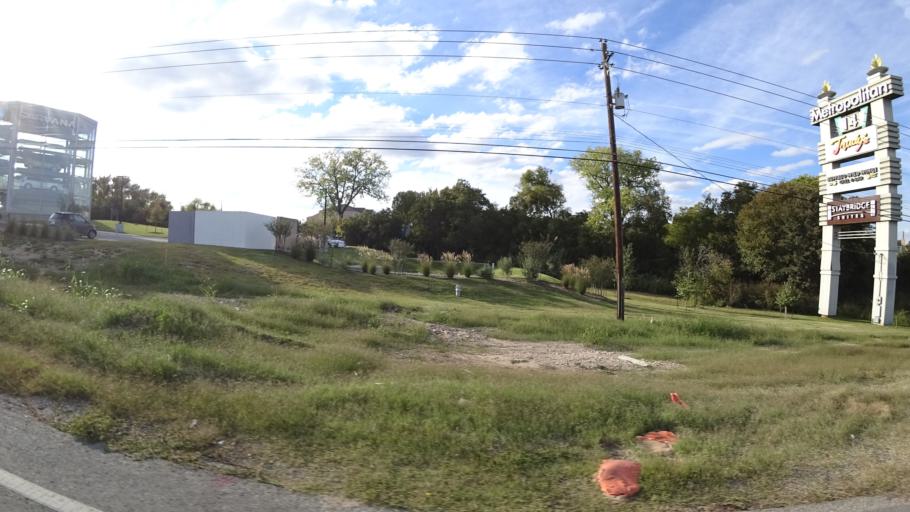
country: US
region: Texas
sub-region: Travis County
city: Onion Creek
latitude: 30.1962
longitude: -97.7664
